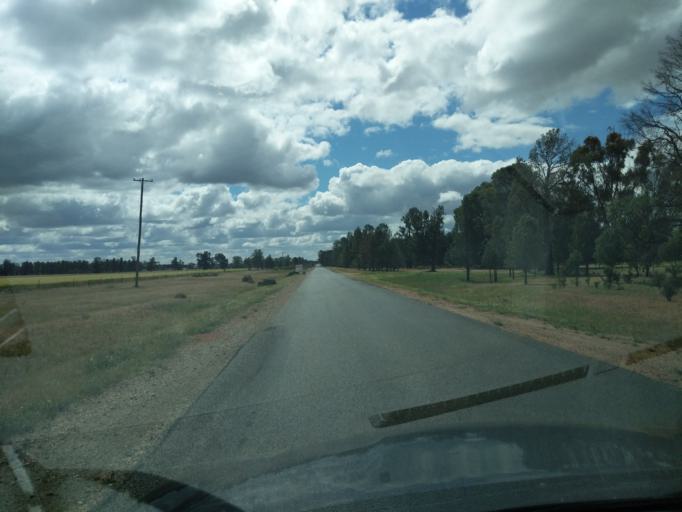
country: AU
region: New South Wales
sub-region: Coolamon
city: Coolamon
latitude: -34.8547
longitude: 146.8991
